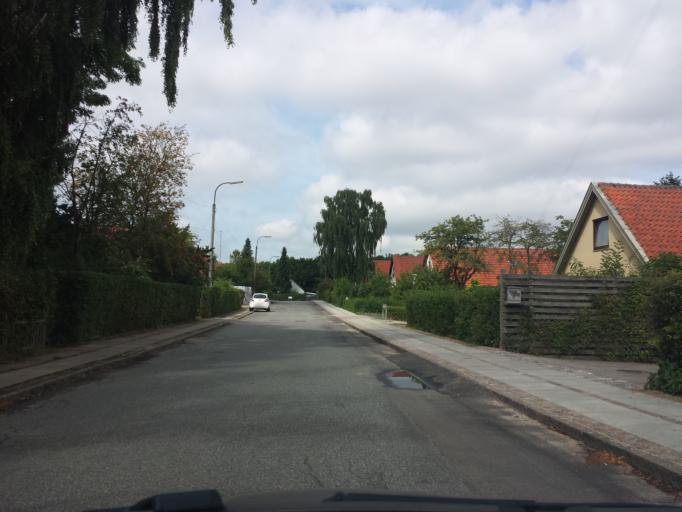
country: DK
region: Capital Region
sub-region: Herlev Kommune
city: Herlev
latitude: 55.7126
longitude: 12.4042
